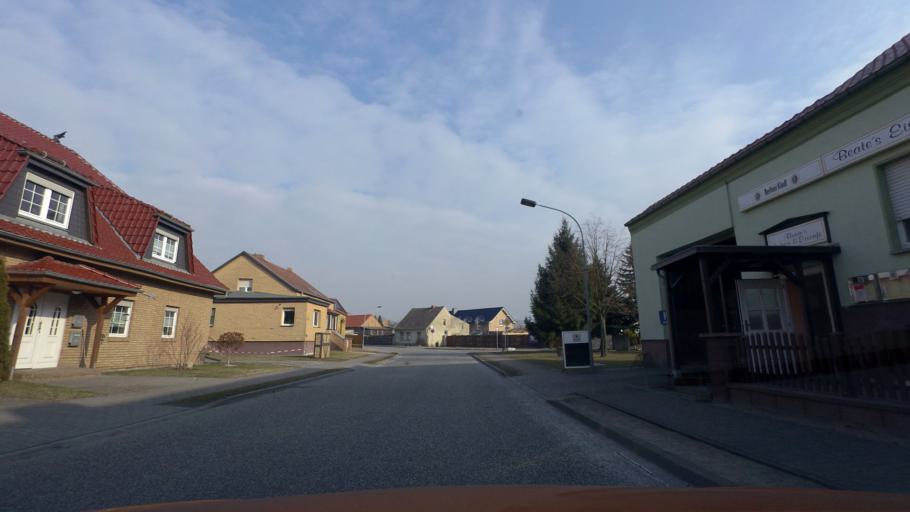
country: DE
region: Brandenburg
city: Trebbin
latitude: 52.2279
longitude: 13.3142
